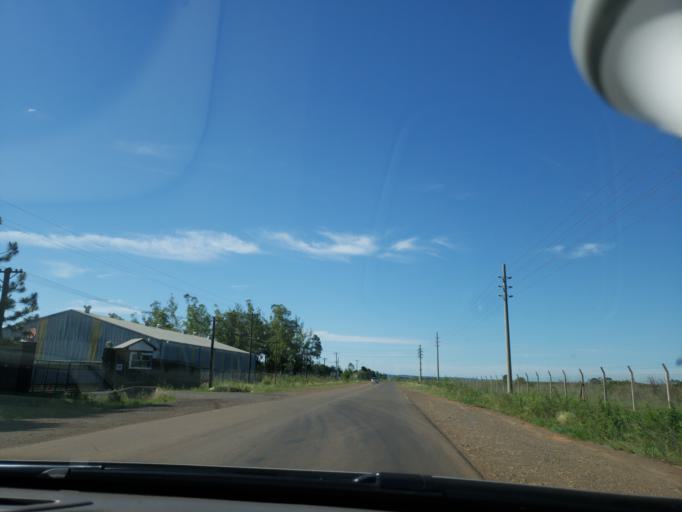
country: AR
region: Misiones
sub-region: Departamento de Capital
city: Posadas
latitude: -27.3887
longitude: -55.9750
